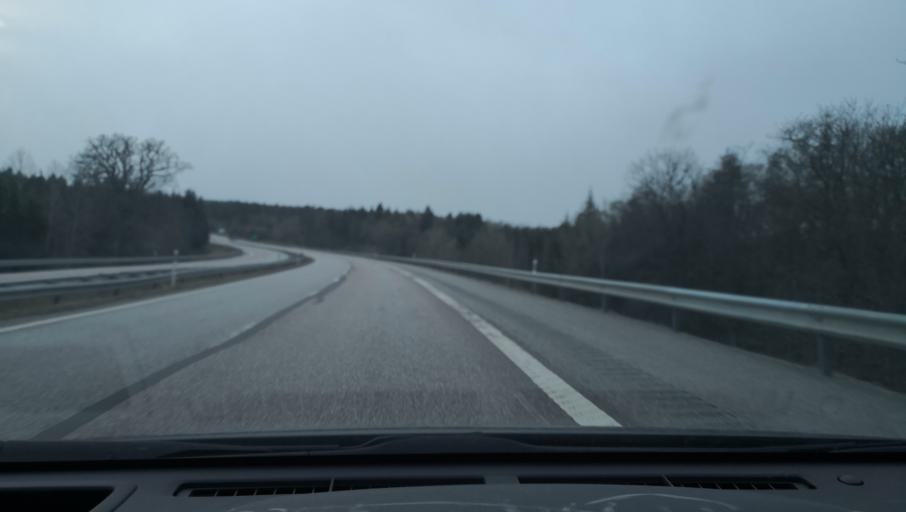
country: SE
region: Soedermanland
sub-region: Eskilstuna Kommun
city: Arla
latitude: 59.3739
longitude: 16.8361
